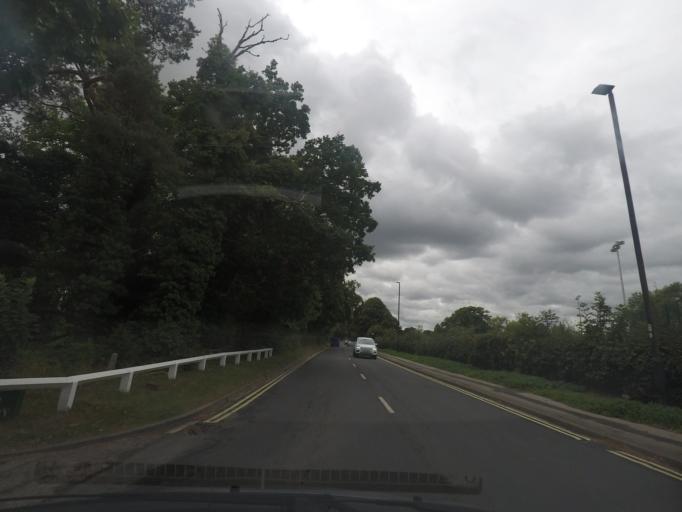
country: GB
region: England
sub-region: City of York
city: Heslington
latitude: 53.9423
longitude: -1.0558
